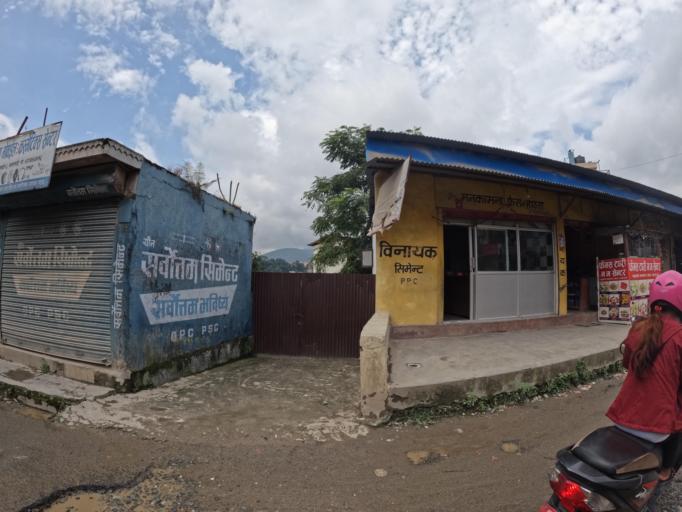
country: NP
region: Central Region
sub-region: Bagmati Zone
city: Kathmandu
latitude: 27.7517
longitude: 85.3176
